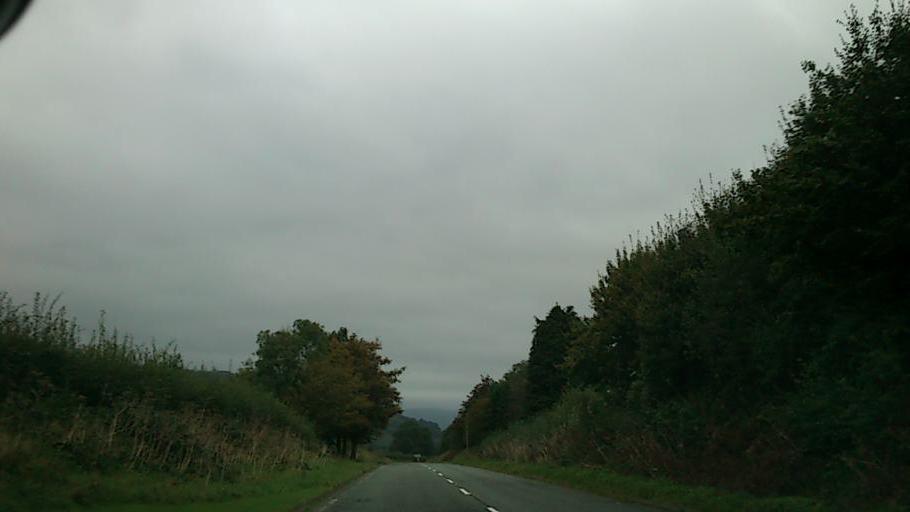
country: GB
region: Wales
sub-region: Gwynedd
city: Corris
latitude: 52.6672
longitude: -3.7076
